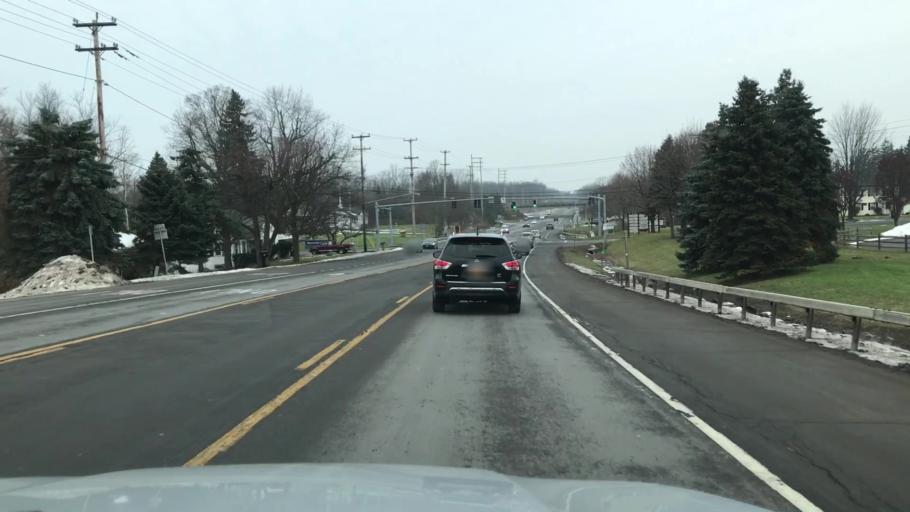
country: US
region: New York
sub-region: Erie County
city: Orchard Park
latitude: 42.7633
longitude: -78.7598
